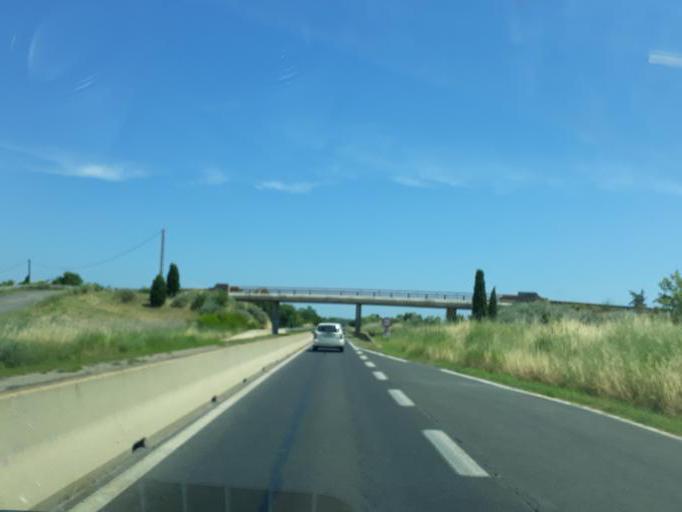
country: FR
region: Languedoc-Roussillon
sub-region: Departement de l'Herault
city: Vias
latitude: 43.3090
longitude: 3.4066
